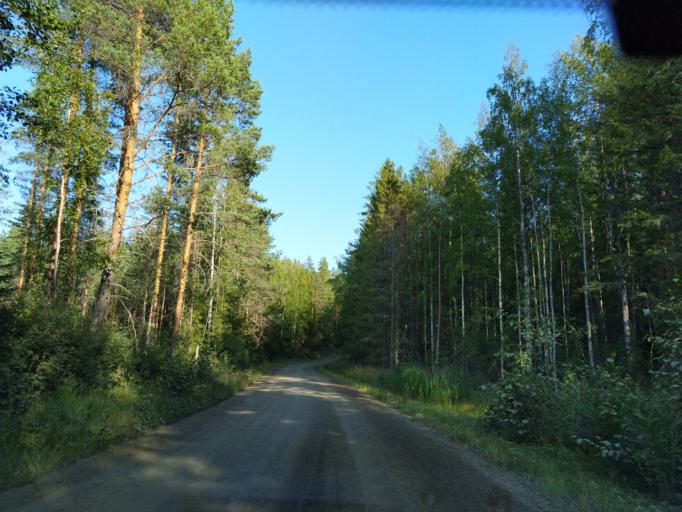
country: FI
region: Central Finland
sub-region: Jaemsae
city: Kuhmoinen
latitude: 61.6820
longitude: 24.9762
